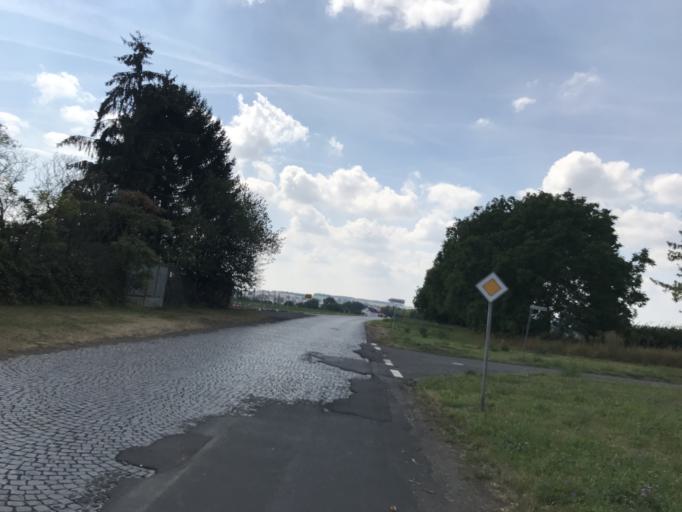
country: DE
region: Hesse
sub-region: Regierungsbezirk Darmstadt
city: Wolfersheim
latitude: 50.4450
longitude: 8.8462
